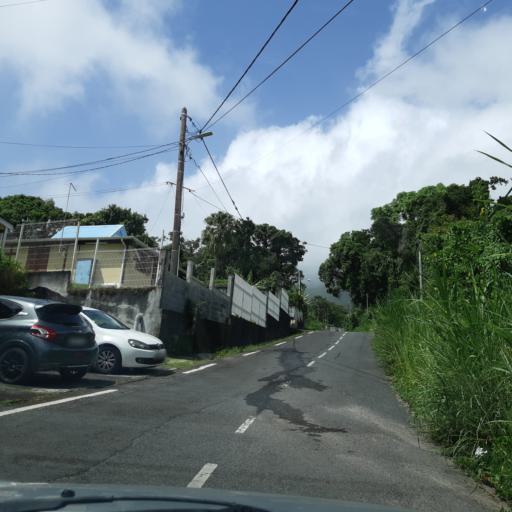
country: GP
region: Guadeloupe
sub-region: Guadeloupe
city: Saint-Claude
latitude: 16.0298
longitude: -61.6890
